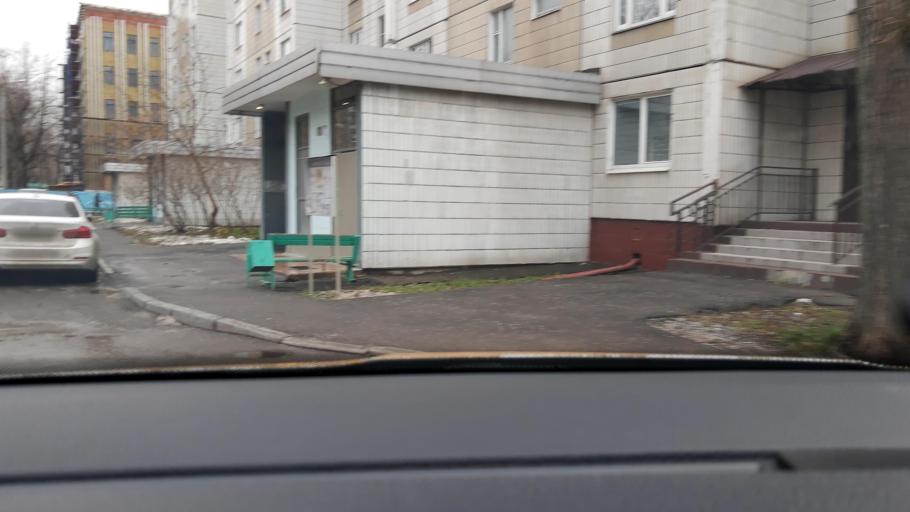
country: RU
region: Moscow
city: Ryazanskiy
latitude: 55.7351
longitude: 37.7492
